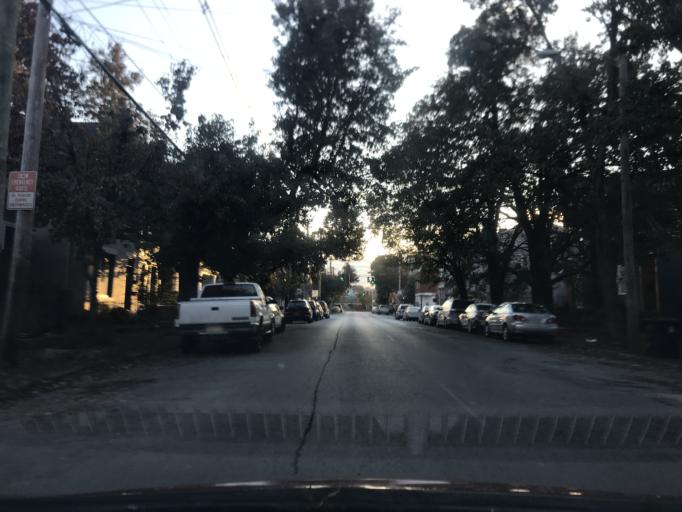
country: US
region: Kentucky
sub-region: Jefferson County
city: Louisville
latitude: 38.2468
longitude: -85.7380
